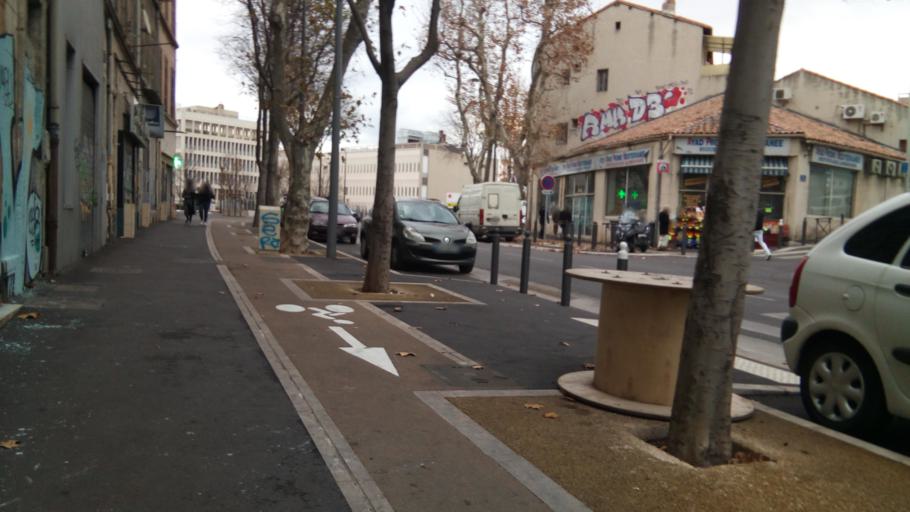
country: FR
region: Provence-Alpes-Cote d'Azur
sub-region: Departement des Bouches-du-Rhone
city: Marseille 03
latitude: 43.3144
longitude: 5.3712
